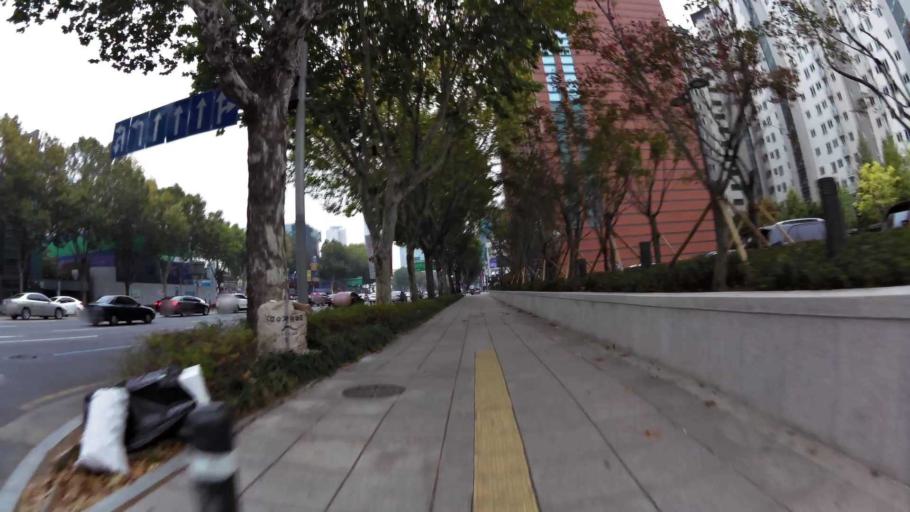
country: KR
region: Daegu
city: Daegu
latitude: 35.8595
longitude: 128.6163
